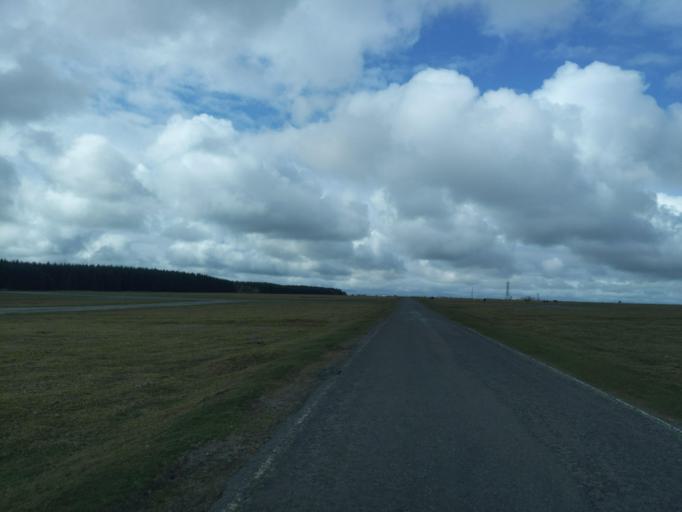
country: GB
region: England
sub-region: Cornwall
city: Camelford
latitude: 50.6322
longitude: -4.6094
